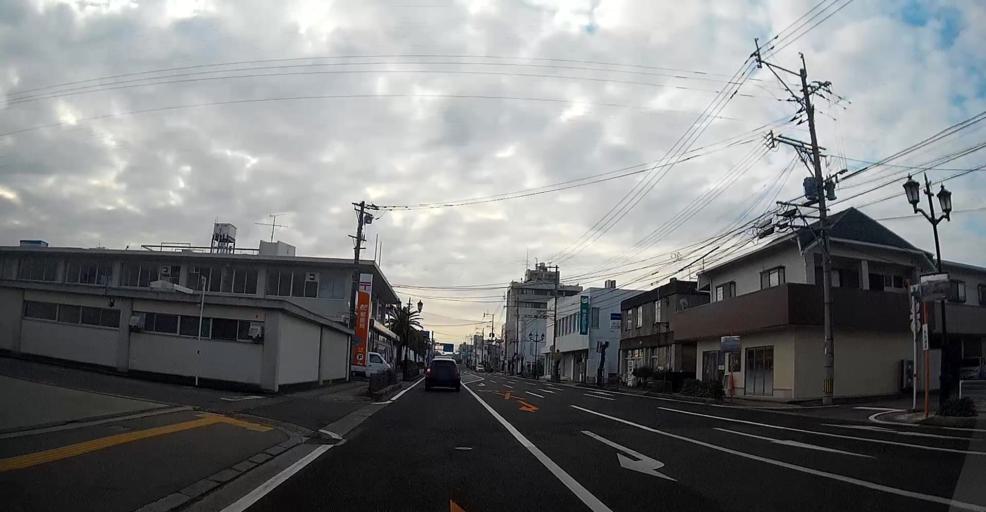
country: JP
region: Kumamoto
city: Hondo
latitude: 32.4593
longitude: 130.1923
